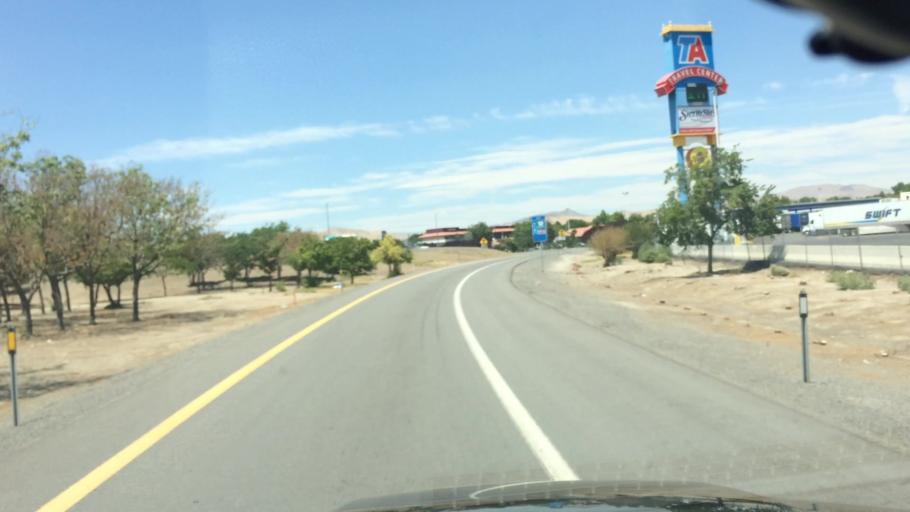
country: US
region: Nevada
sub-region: Washoe County
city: Sparks
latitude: 39.5325
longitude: -119.7357
